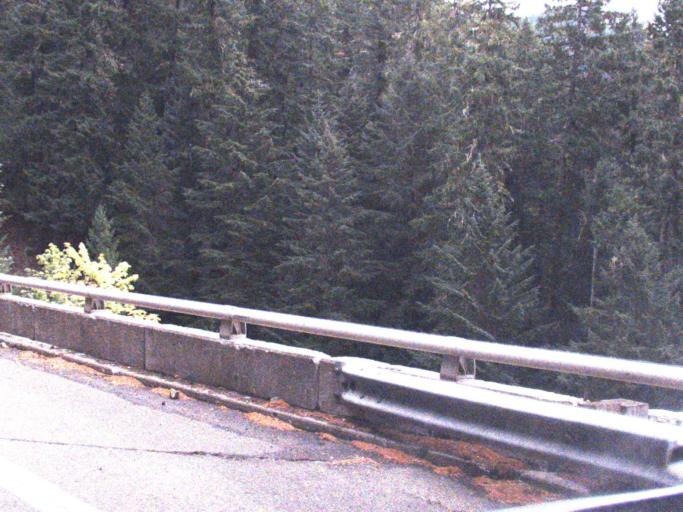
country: US
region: Washington
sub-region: Pierce County
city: Buckley
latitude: 46.6714
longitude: -121.5029
